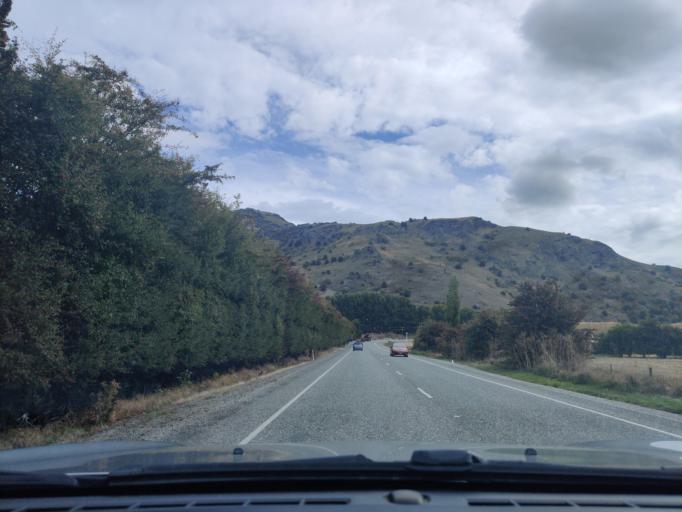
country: NZ
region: Otago
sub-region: Queenstown-Lakes District
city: Arrowtown
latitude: -44.9809
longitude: 168.8411
